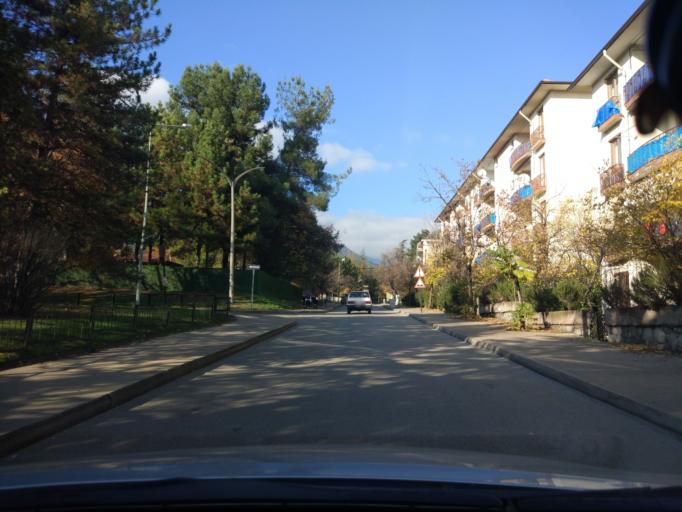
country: TR
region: Karabuk
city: Karabuk
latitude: 41.1987
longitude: 32.6226
